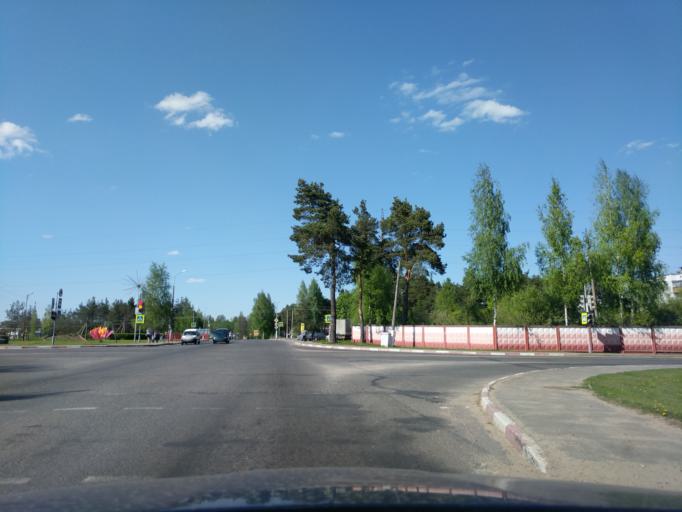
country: BY
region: Vitebsk
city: Pastavy
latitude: 55.1021
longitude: 26.8755
